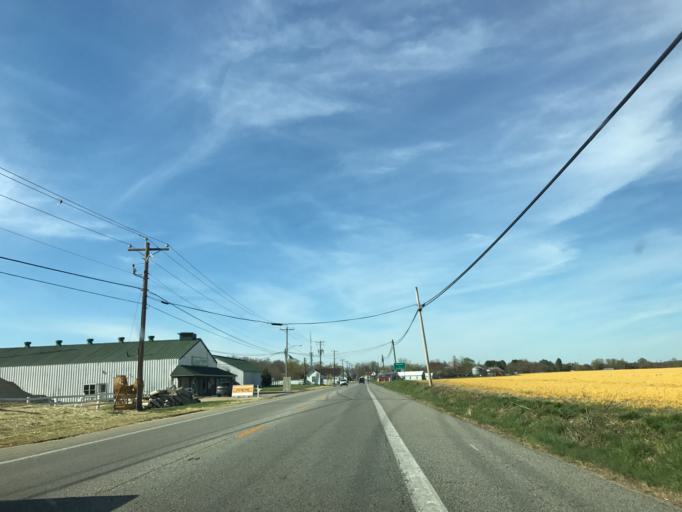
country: US
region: Maryland
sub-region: Caroline County
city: Greensboro
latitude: 39.0293
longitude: -75.7872
